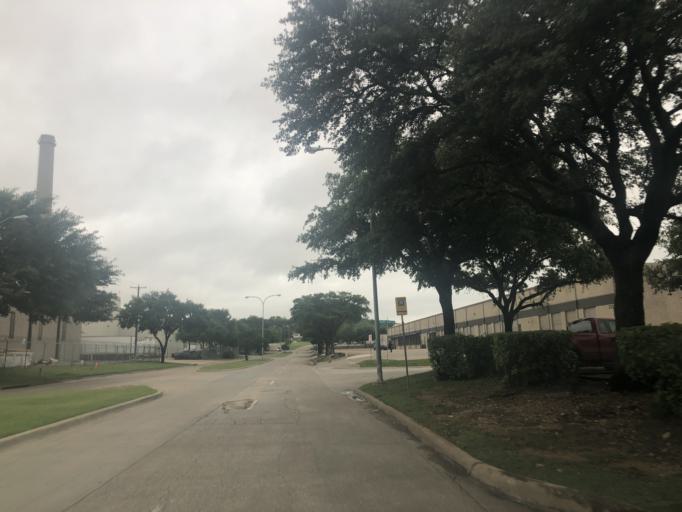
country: US
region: Texas
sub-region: Dallas County
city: Cockrell Hill
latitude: 32.7729
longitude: -96.8581
